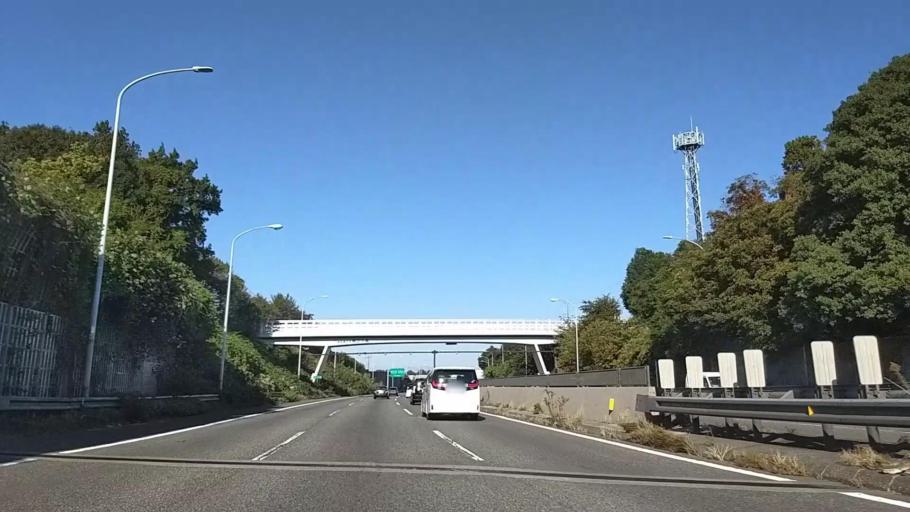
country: JP
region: Kanagawa
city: Yokohama
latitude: 35.4561
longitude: 139.5495
